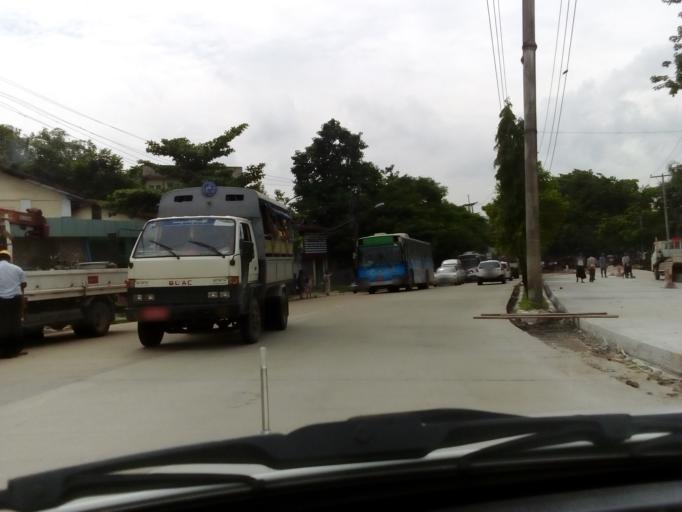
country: MM
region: Yangon
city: Yangon
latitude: 16.8669
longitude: 96.1381
